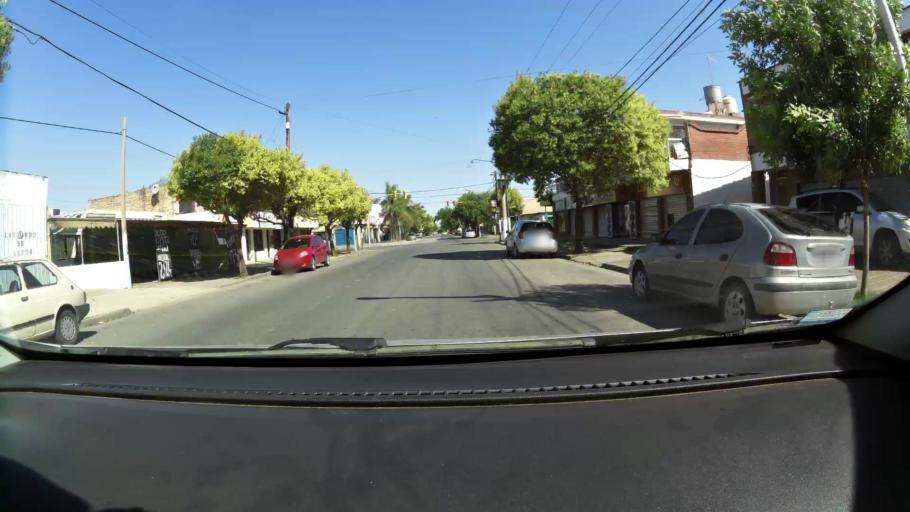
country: AR
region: Cordoba
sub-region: Departamento de Capital
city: Cordoba
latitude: -31.3629
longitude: -64.1704
